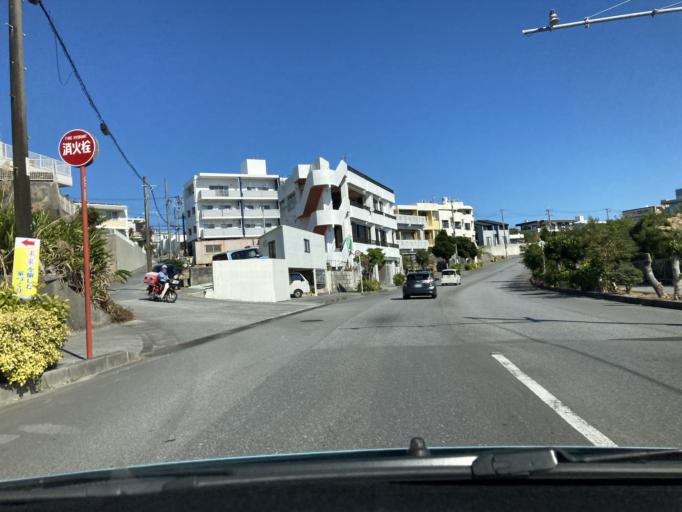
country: JP
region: Okinawa
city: Gushikawa
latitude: 26.3511
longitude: 127.8386
